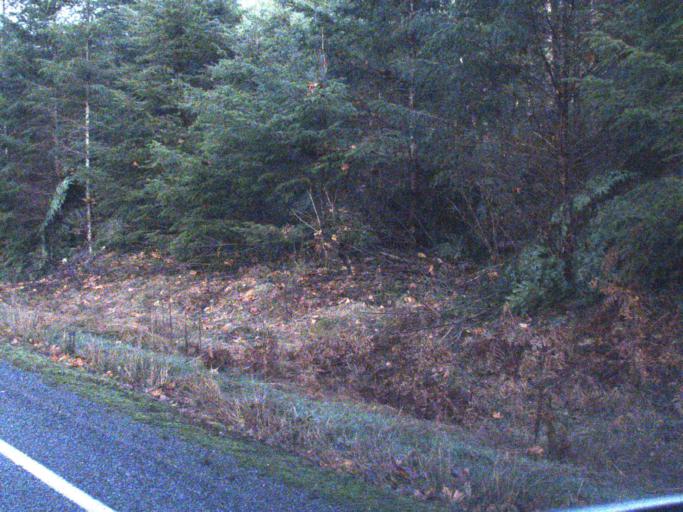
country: US
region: Washington
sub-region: Snohomish County
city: Darrington
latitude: 48.3990
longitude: -121.5522
